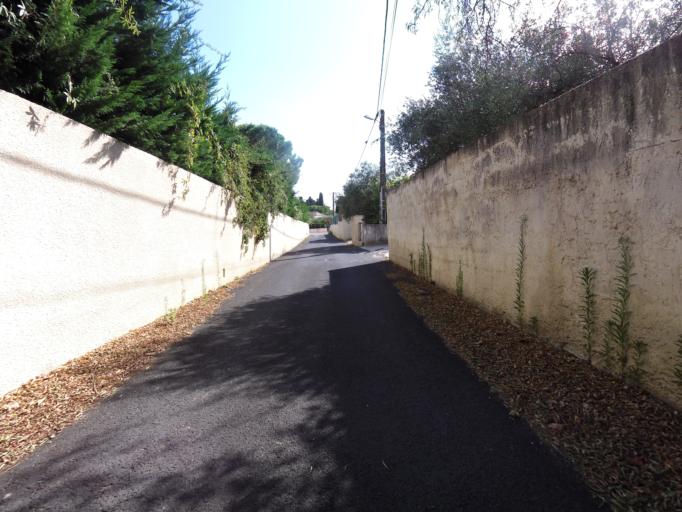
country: FR
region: Languedoc-Roussillon
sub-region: Departement du Gard
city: Gallargues-le-Montueux
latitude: 43.7237
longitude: 4.1673
